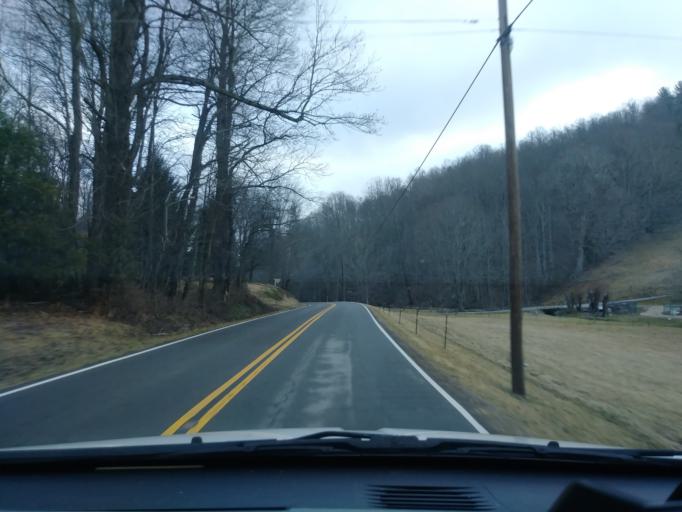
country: US
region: Tennessee
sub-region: Unicoi County
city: Unicoi
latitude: 36.1861
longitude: -82.2511
